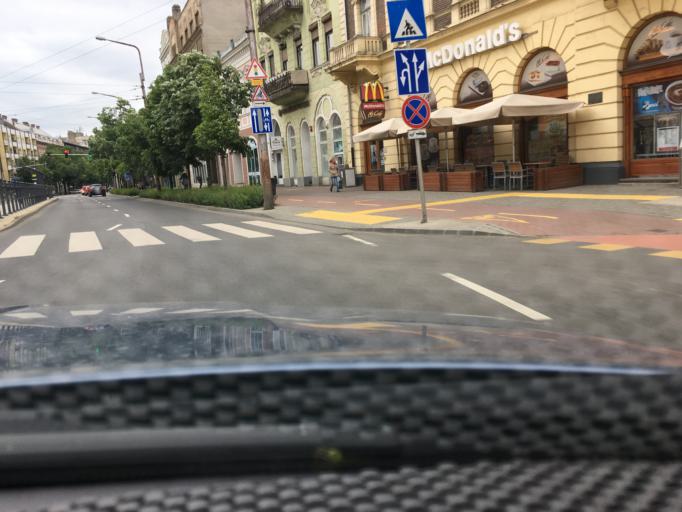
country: HU
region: Hajdu-Bihar
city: Debrecen
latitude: 47.5273
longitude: 21.6259
